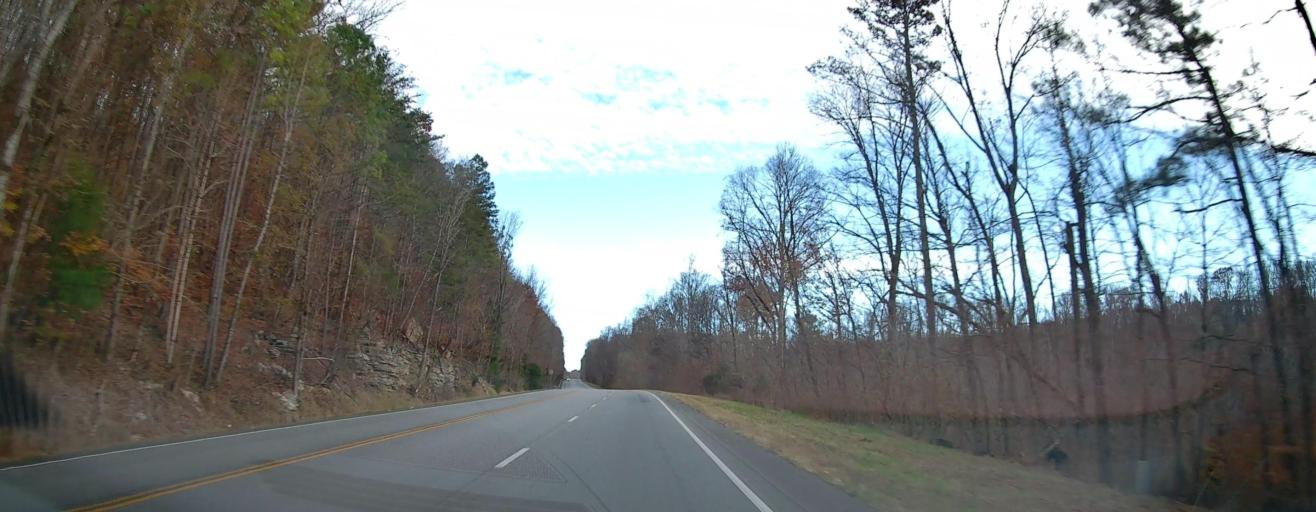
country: US
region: Alabama
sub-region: Marshall County
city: Arab
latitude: 34.3621
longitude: -86.6317
